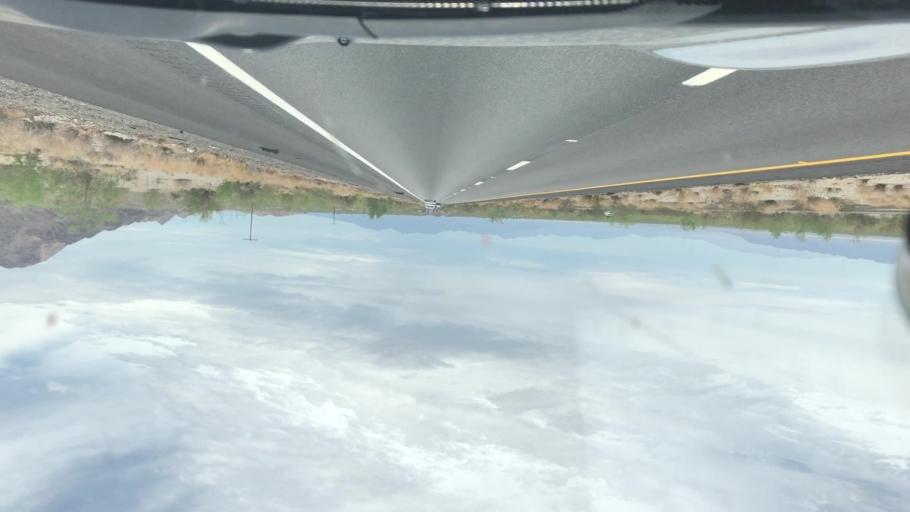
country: US
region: California
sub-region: Imperial County
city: Niland
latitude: 33.6888
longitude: -115.5132
